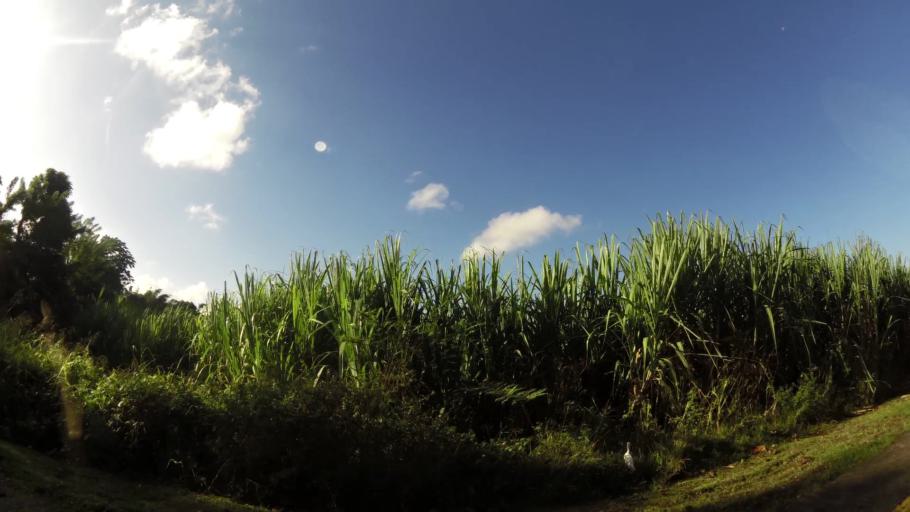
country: MQ
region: Martinique
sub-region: Martinique
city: Le Lamentin
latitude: 14.6313
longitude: -61.0310
